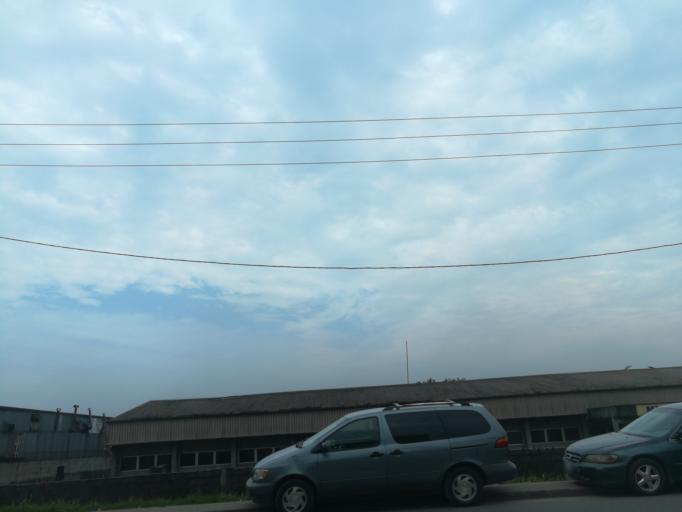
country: NG
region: Rivers
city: Port Harcourt
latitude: 4.8465
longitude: 6.9811
